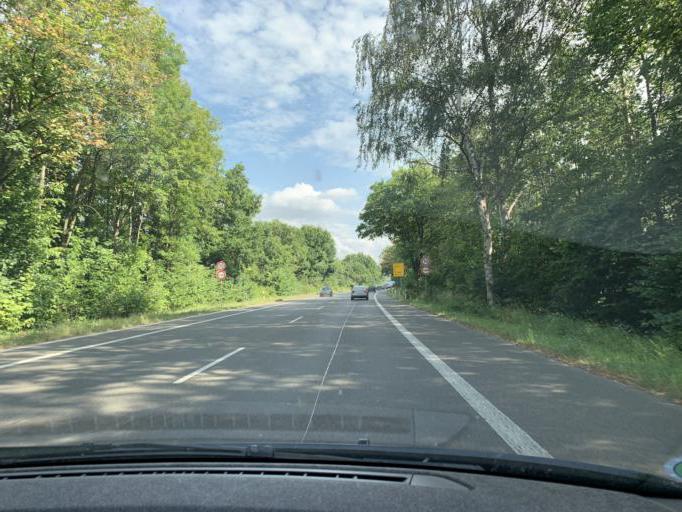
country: DE
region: North Rhine-Westphalia
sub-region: Regierungsbezirk Koln
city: Inden
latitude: 50.8819
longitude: 6.4104
